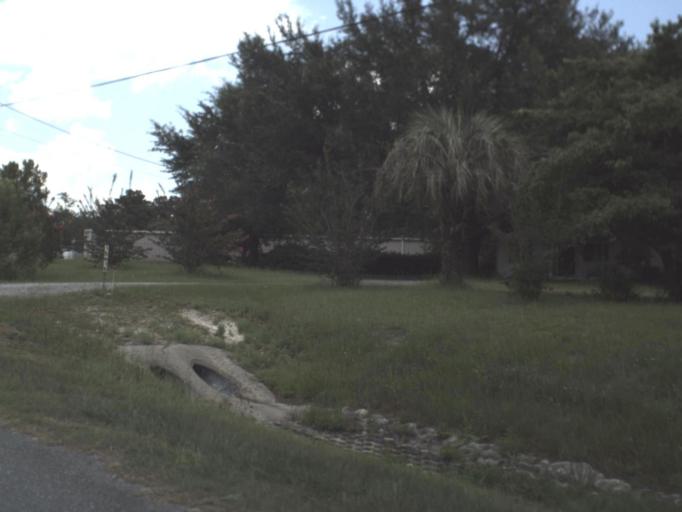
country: US
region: Florida
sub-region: Baker County
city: Macclenny
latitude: 30.3540
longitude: -82.1297
